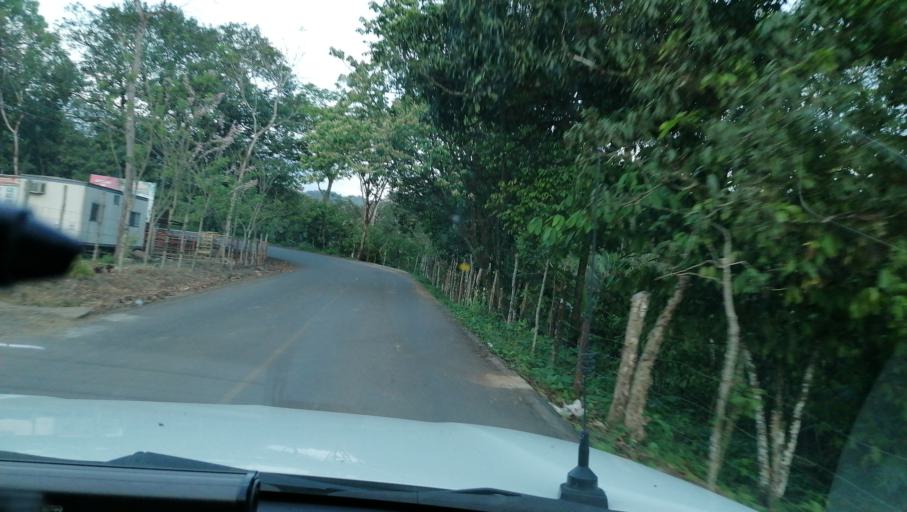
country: MX
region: Chiapas
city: Ostuacan
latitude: 17.4193
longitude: -93.3391
